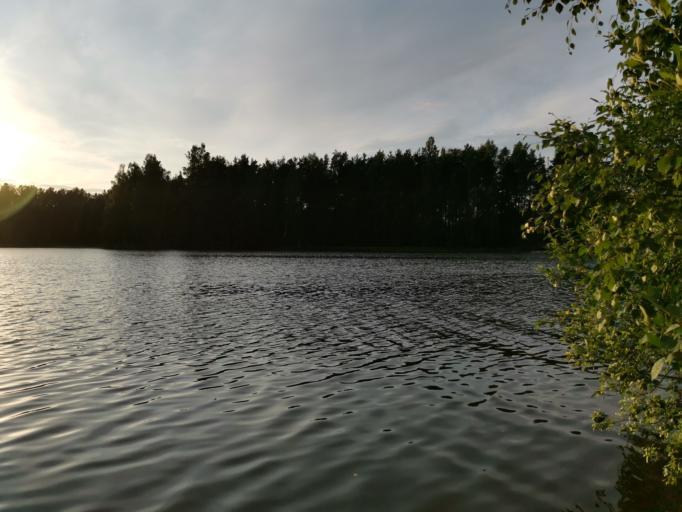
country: RU
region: St.-Petersburg
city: Pargolovo
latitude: 60.1133
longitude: 30.3023
